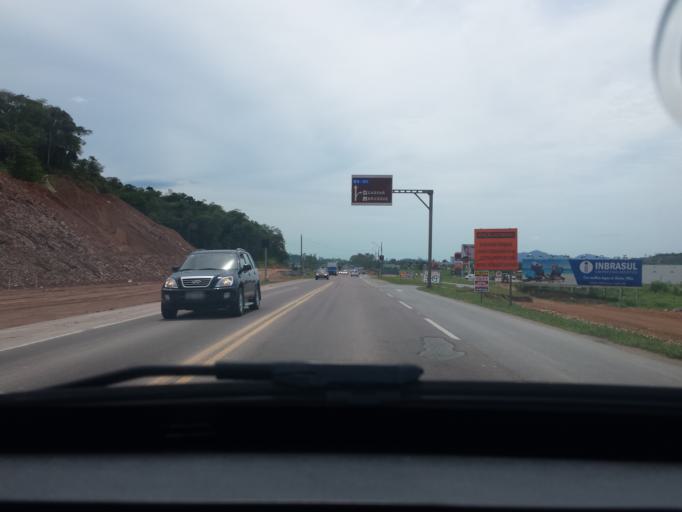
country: BR
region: Santa Catarina
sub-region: Gaspar
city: Gaspar
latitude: -26.9133
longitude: -48.9628
